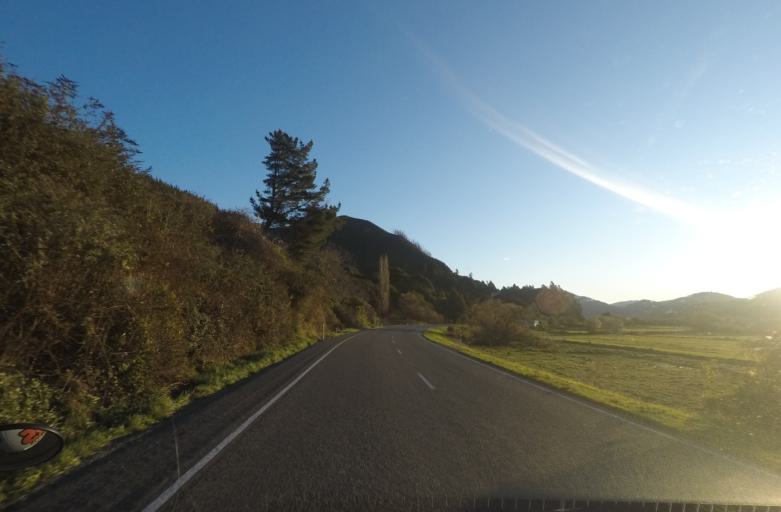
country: NZ
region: Marlborough
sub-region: Marlborough District
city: Picton
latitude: -41.2881
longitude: 173.7027
